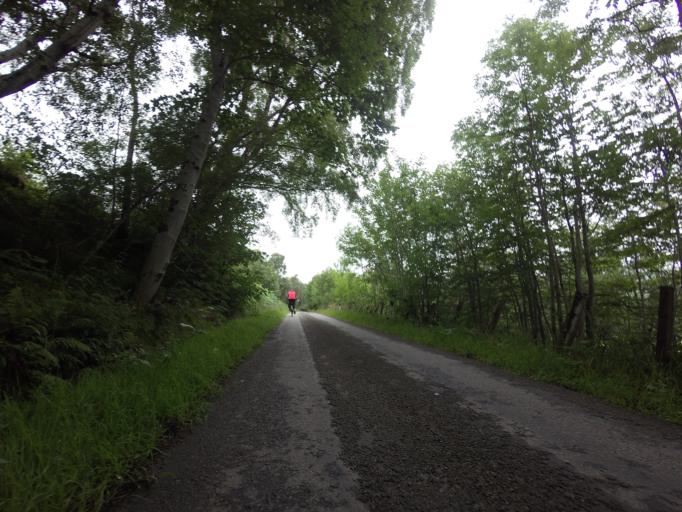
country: GB
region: Scotland
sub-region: Highland
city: Alness
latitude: 57.8941
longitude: -4.3755
